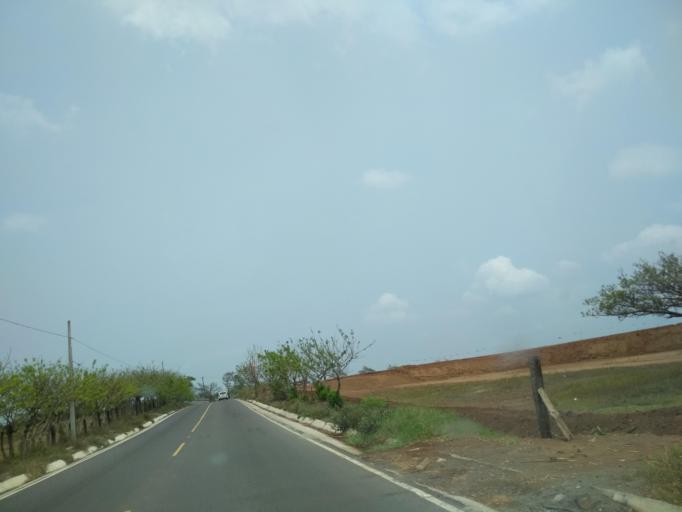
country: MX
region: Veracruz
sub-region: Veracruz
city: Delfino Victoria (Santa Fe)
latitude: 19.1737
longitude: -96.2717
